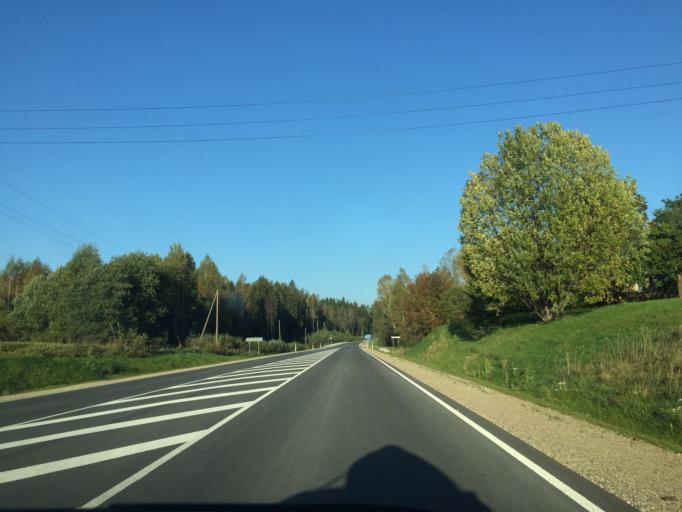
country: LV
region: Vecpiebalga
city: Vecpiebalga
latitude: 57.0780
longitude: 25.7616
